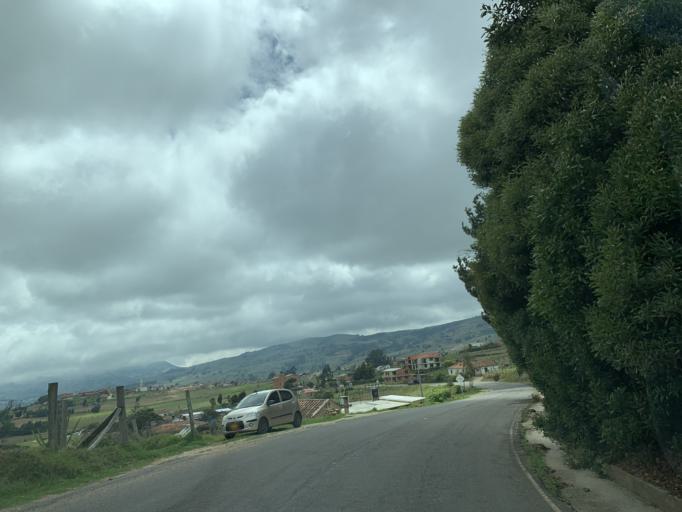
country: CO
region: Boyaca
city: Tunja
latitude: 5.5796
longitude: -73.3578
